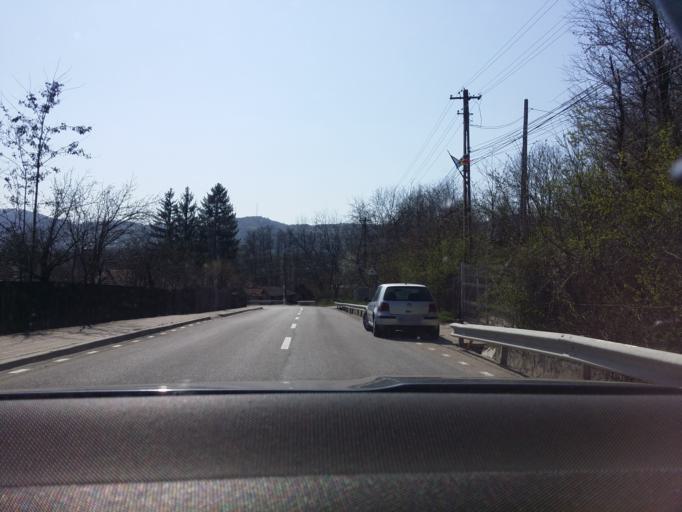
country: RO
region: Prahova
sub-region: Comuna Cornu
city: Cornu de Jos
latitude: 45.1459
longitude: 25.7137
